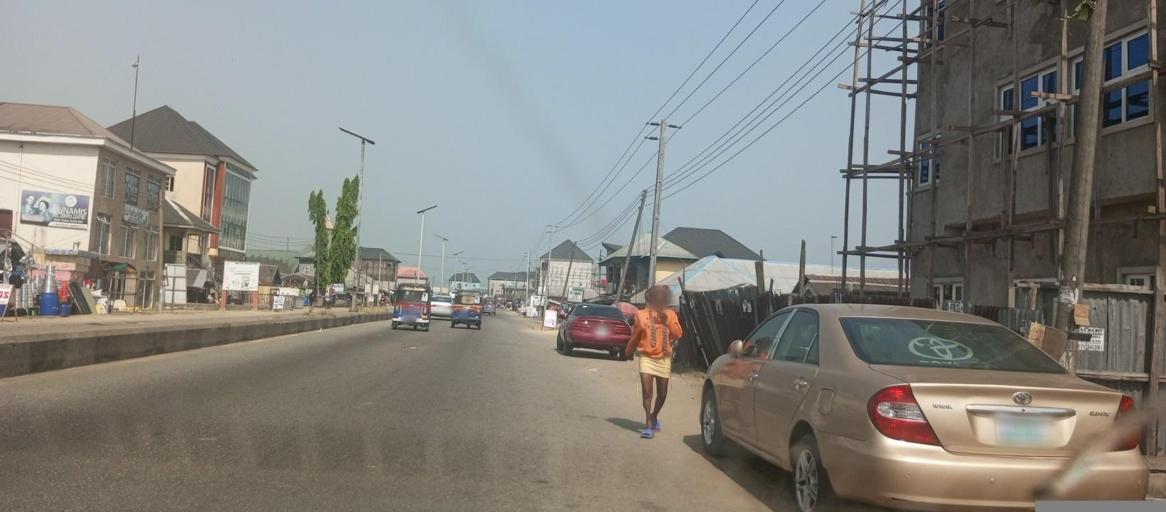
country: NG
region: Bayelsa
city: Yenagoa
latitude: 4.9568
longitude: 6.3622
